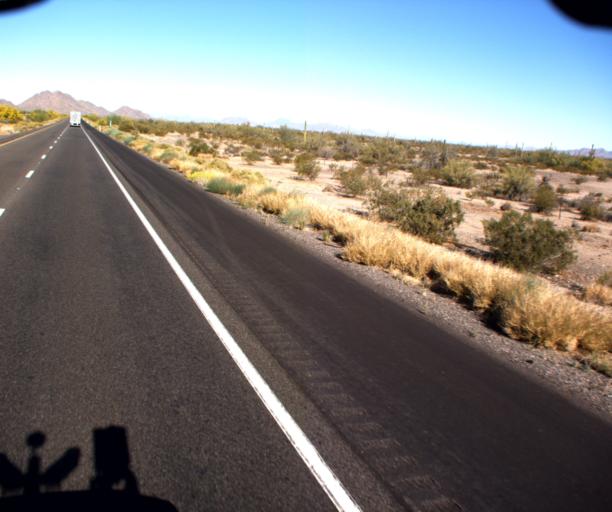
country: US
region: Arizona
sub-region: Maricopa County
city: Gila Bend
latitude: 32.8938
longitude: -112.4935
